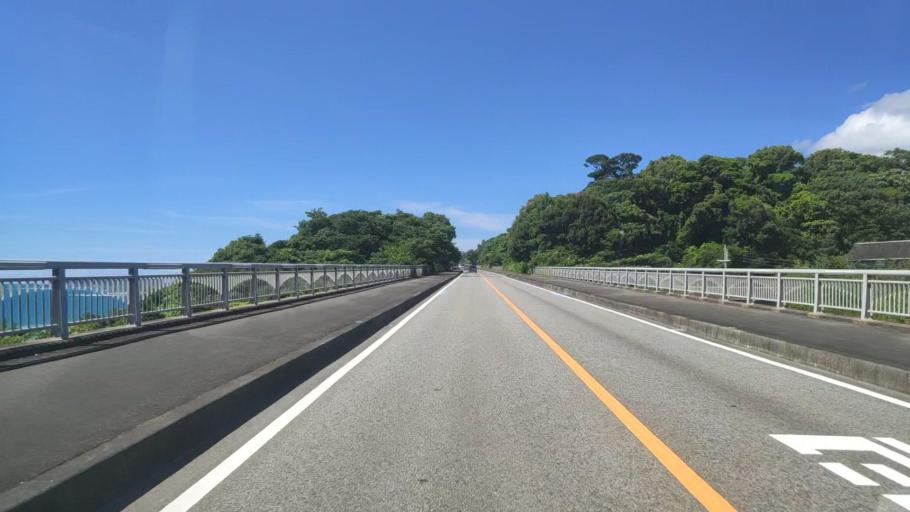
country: JP
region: Wakayama
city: Shingu
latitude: 33.7108
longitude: 135.9978
